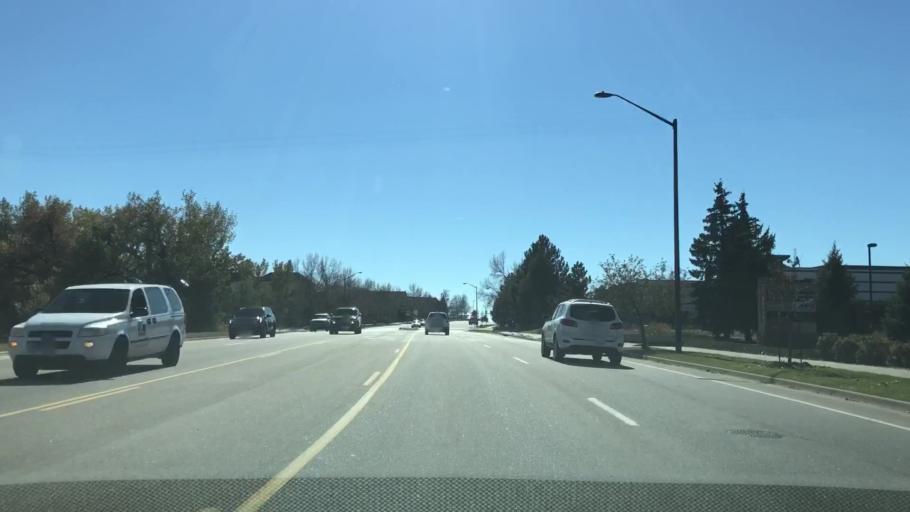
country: US
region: Colorado
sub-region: Larimer County
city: Fort Collins
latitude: 40.5360
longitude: -105.0738
